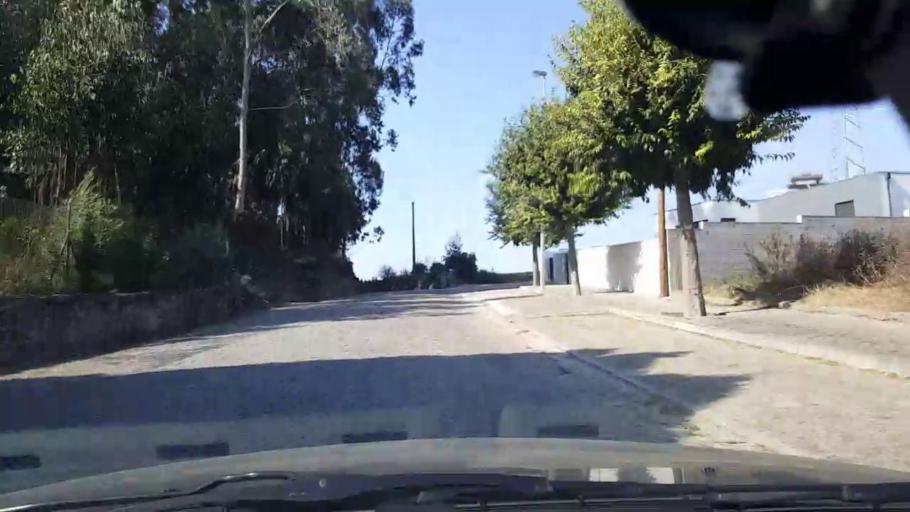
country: PT
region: Porto
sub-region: Vila do Conde
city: Arvore
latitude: 41.3551
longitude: -8.7075
